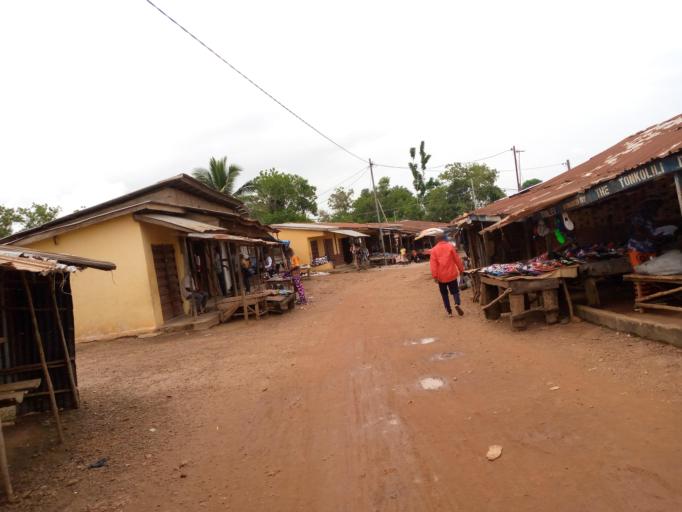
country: SL
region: Northern Province
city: Magburaka
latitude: 8.7223
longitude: -11.9513
